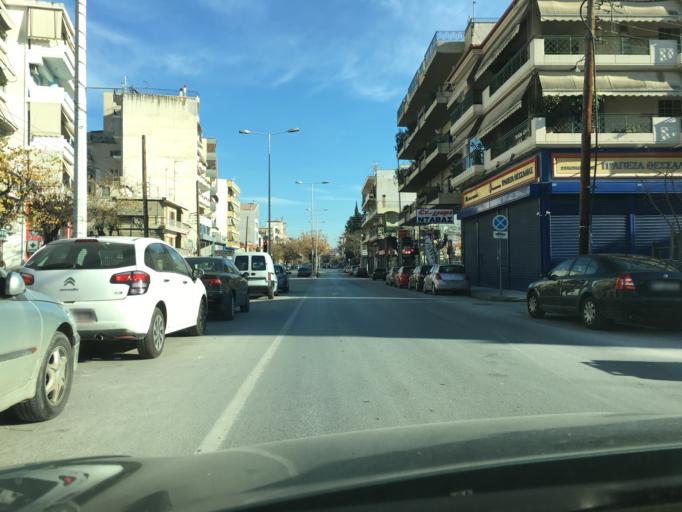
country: GR
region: Thessaly
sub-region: Nomos Larisis
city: Larisa
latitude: 39.6320
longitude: 22.4124
